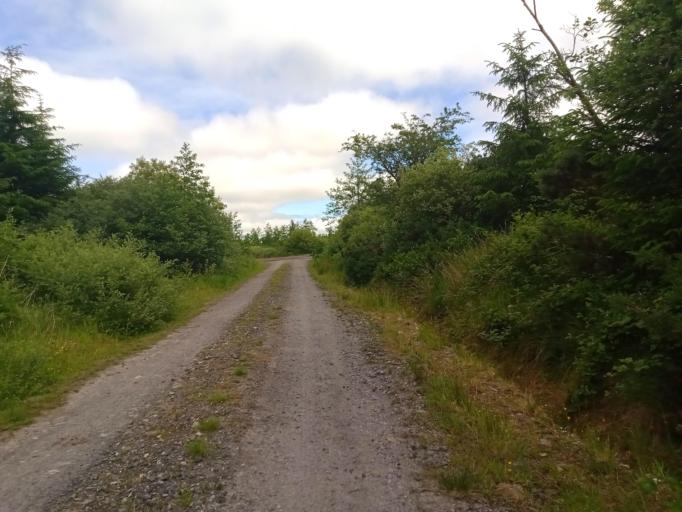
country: IE
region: Leinster
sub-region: Kilkenny
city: Ballyragget
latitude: 52.7908
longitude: -7.4455
